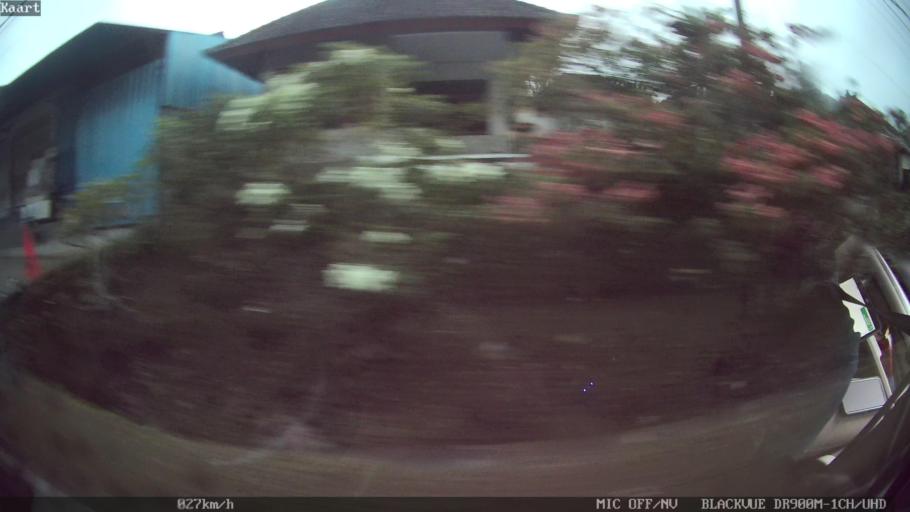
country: ID
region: Bali
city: Banjar Buahan
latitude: -8.4018
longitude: 115.2480
